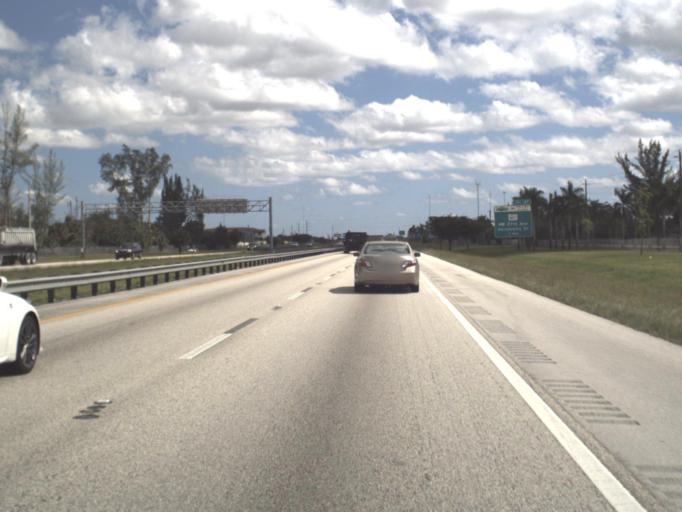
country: US
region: Florida
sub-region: Miami-Dade County
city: Lake Lucerne
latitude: 25.9715
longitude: -80.2722
